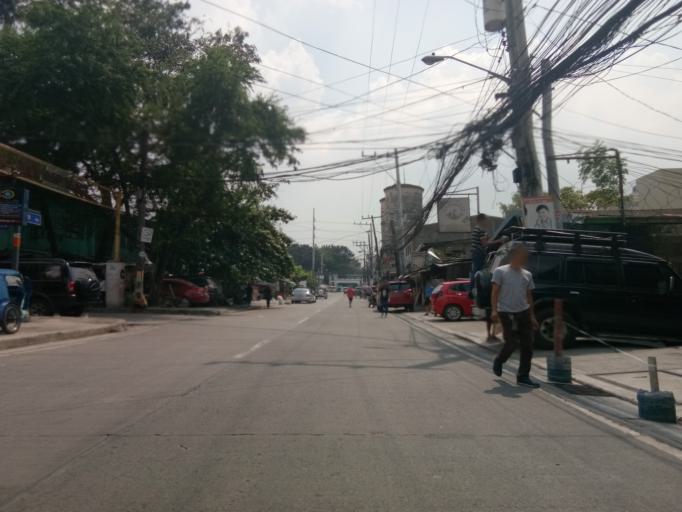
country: PH
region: Metro Manila
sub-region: Pasig
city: Pasig City
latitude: 14.6142
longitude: 121.0621
